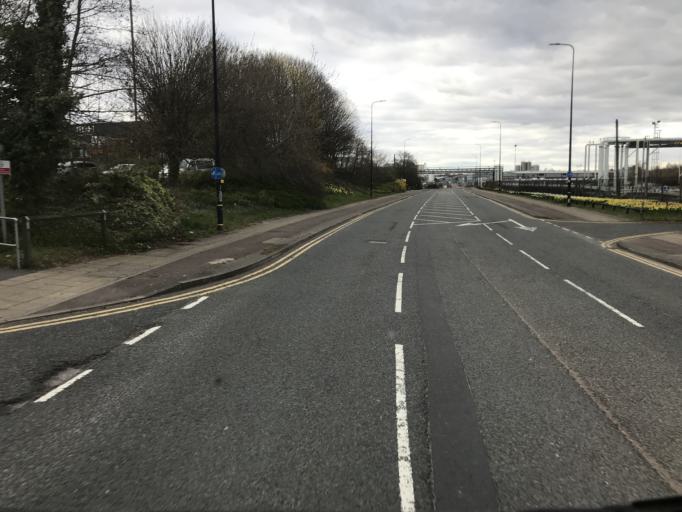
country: GB
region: England
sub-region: Trafford
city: Trafford Park
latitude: 53.4715
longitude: -2.3086
